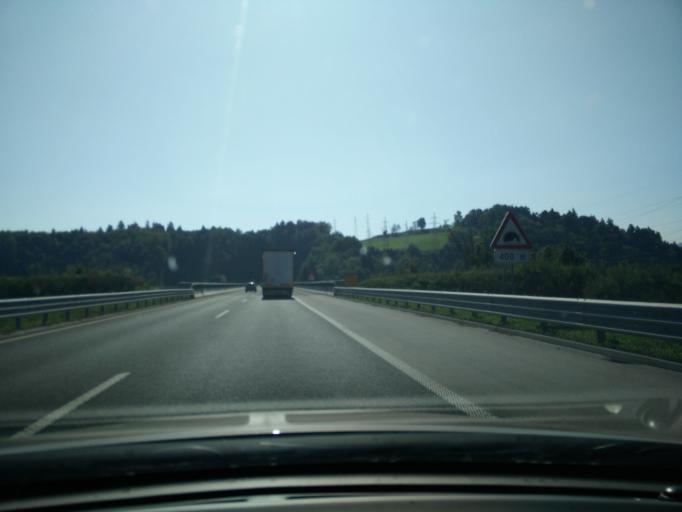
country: SI
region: Trzic
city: Bistrica pri Trzicu
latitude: 46.3209
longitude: 14.2380
